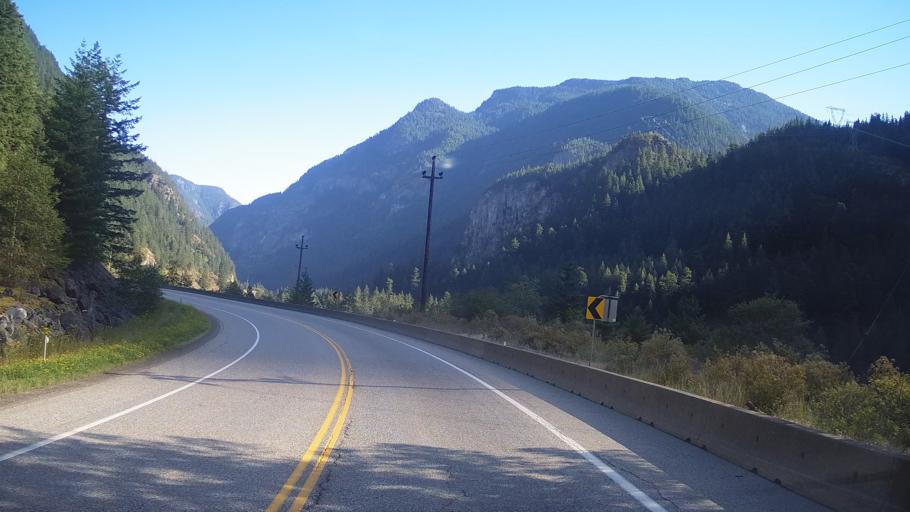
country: CA
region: British Columbia
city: Hope
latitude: 49.5652
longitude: -121.4004
